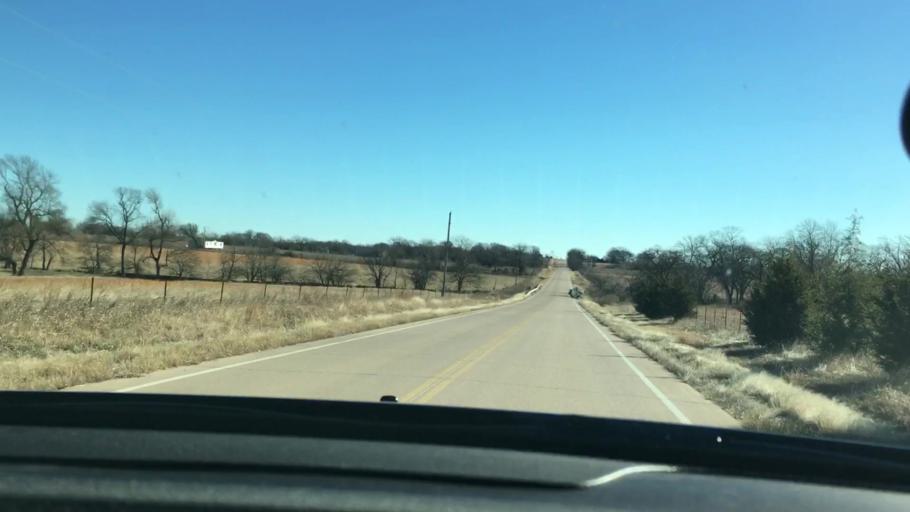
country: US
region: Oklahoma
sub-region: Marshall County
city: Madill
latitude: 34.1144
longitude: -96.7182
